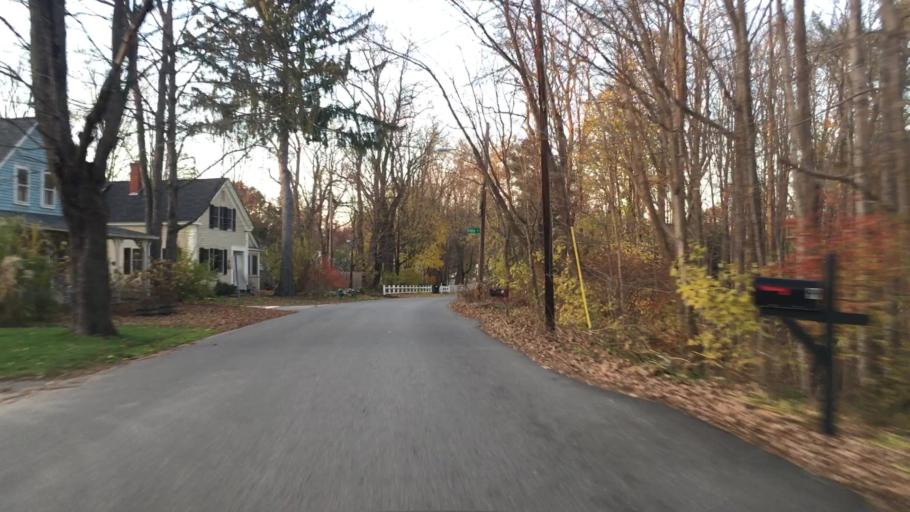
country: US
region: New Hampshire
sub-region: Hillsborough County
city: Milford
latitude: 42.8624
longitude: -71.6233
